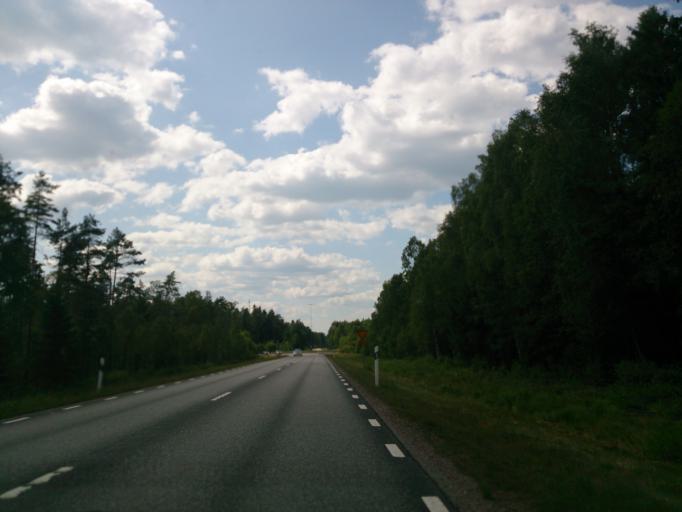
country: SE
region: Joenkoeping
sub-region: Varnamo Kommun
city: Bredaryd
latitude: 57.1690
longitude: 13.7676
